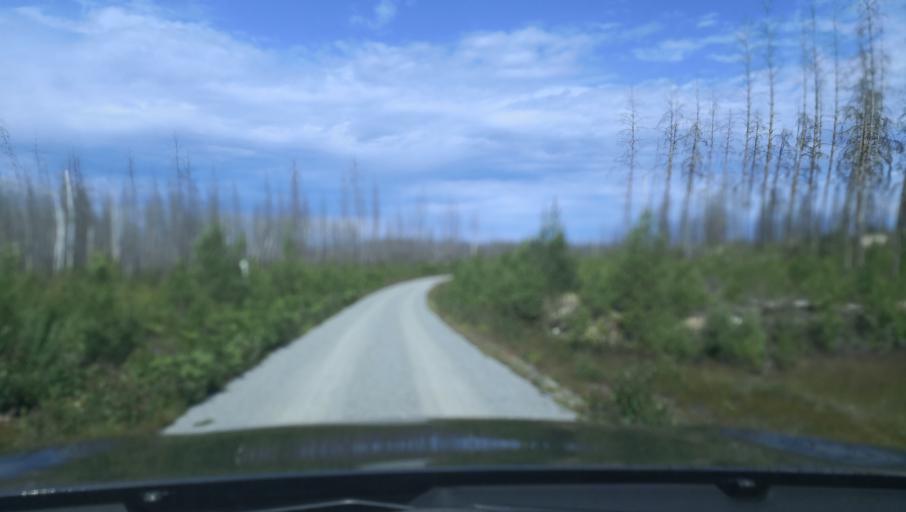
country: SE
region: Vaestmanland
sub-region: Surahammars Kommun
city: Ramnas
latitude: 59.9264
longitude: 16.1687
